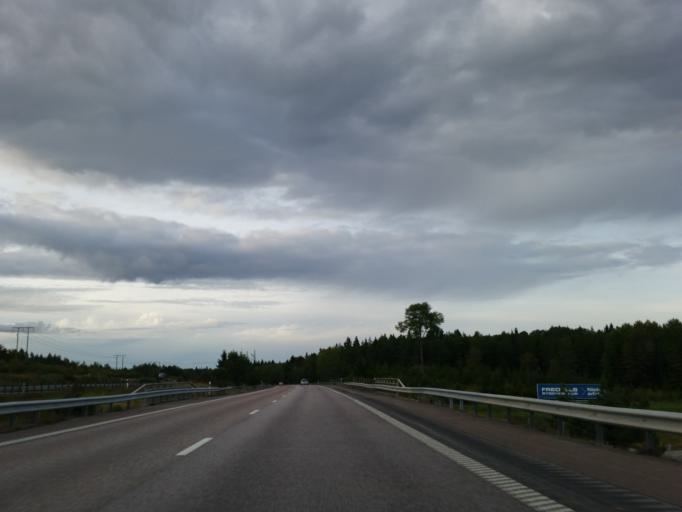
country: SE
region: Stockholm
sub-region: Sigtuna Kommun
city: Marsta
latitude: 59.6841
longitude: 17.8694
